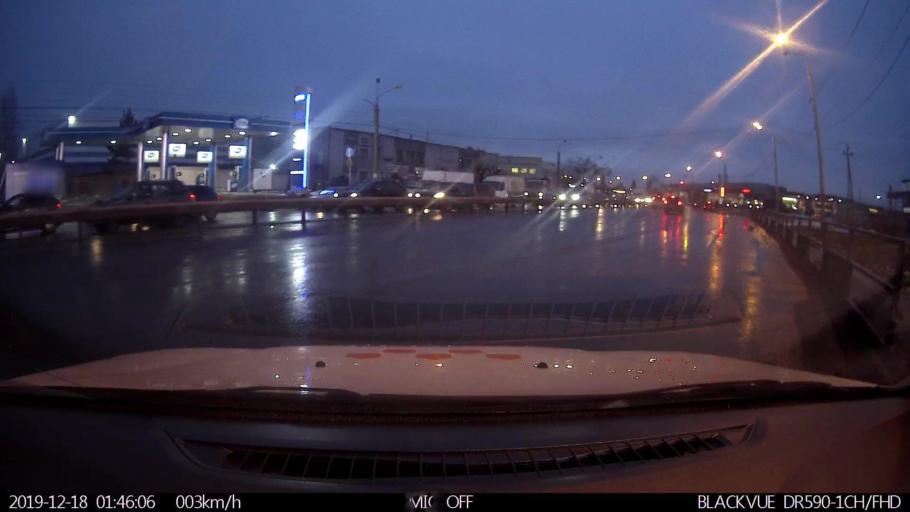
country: RU
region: Nizjnij Novgorod
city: Nizhniy Novgorod
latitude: 56.3114
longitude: 43.8993
